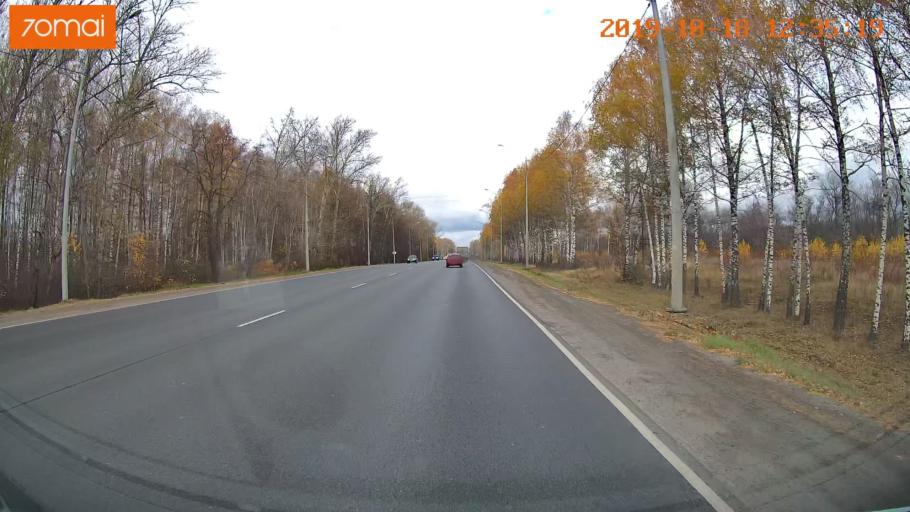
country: RU
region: Rjazan
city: Ryazan'
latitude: 54.6231
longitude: 39.6359
